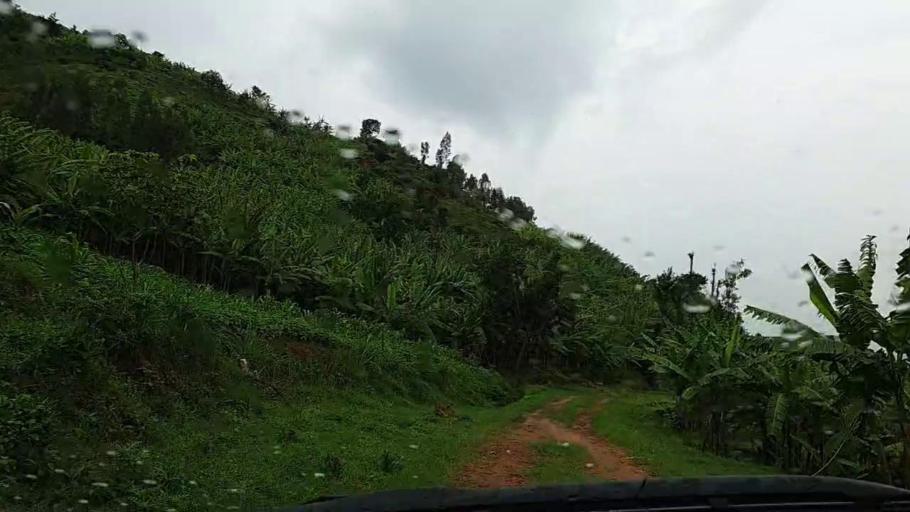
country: RW
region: Kigali
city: Kigali
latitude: -1.9052
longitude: 29.9563
